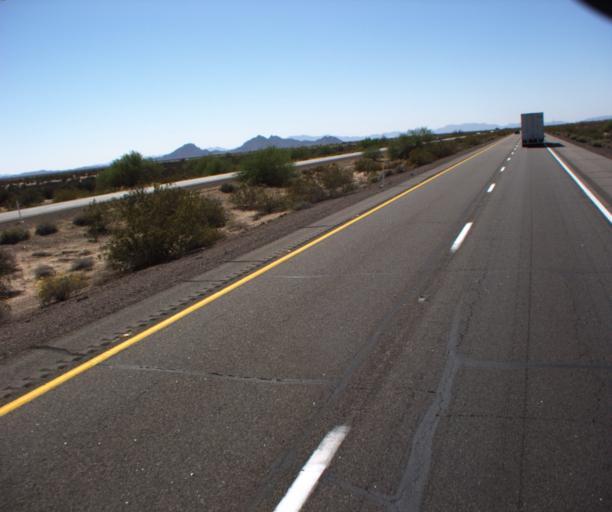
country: US
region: Arizona
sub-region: Yuma County
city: Wellton
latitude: 32.7024
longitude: -113.8963
